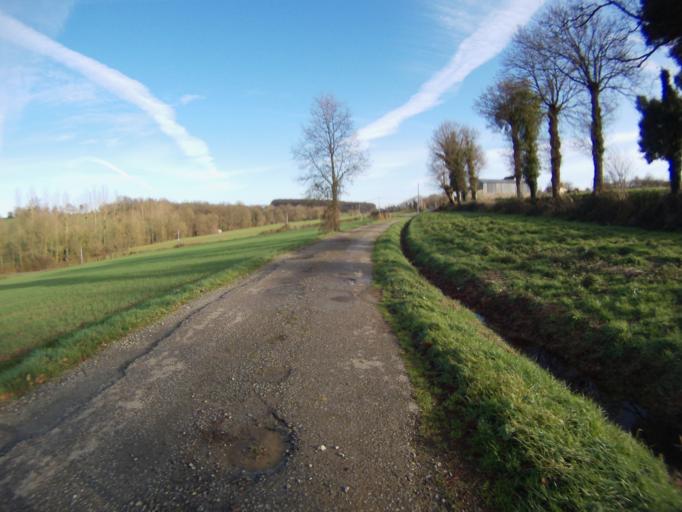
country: FR
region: Brittany
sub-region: Departement d'Ille-et-Vilaine
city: Chanteloup
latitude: 47.9229
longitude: -1.6087
